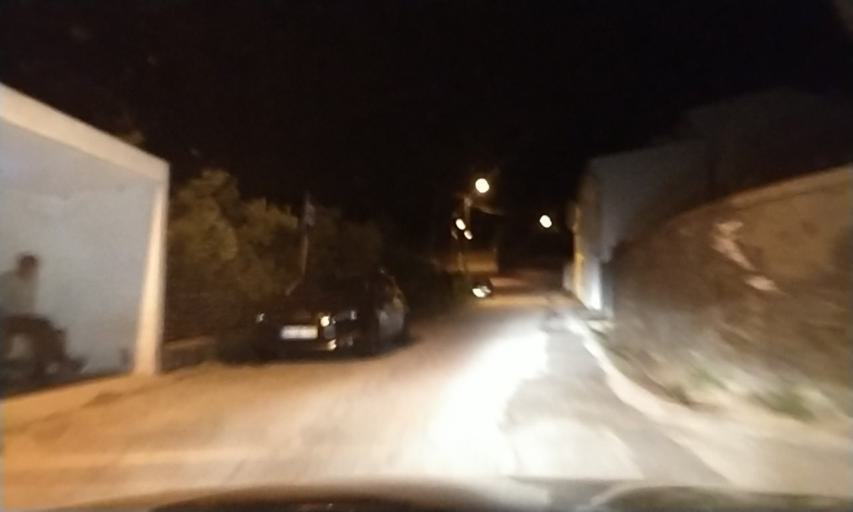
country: PT
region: Vila Real
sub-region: Peso da Regua
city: Godim
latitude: 41.1649
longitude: -7.8182
